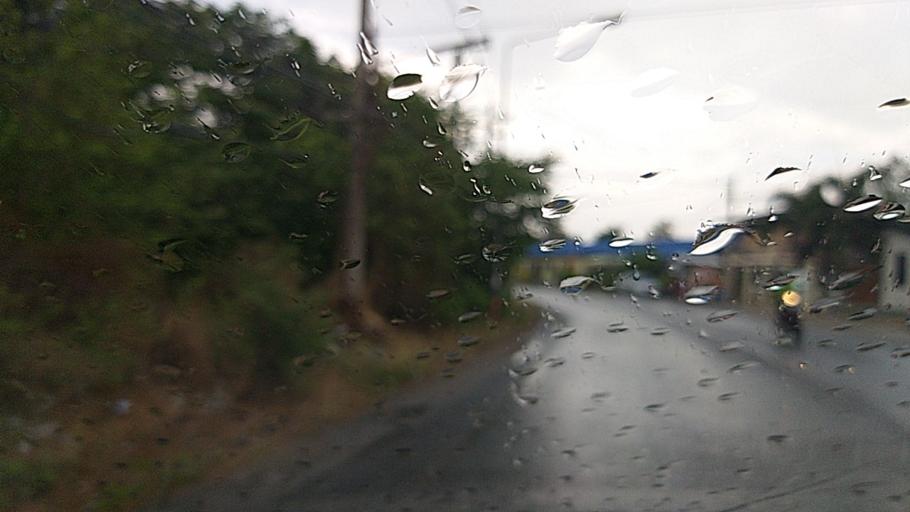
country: TH
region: Phra Nakhon Si Ayutthaya
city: Phra Nakhon Si Ayutthaya
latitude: 14.3406
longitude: 100.5404
